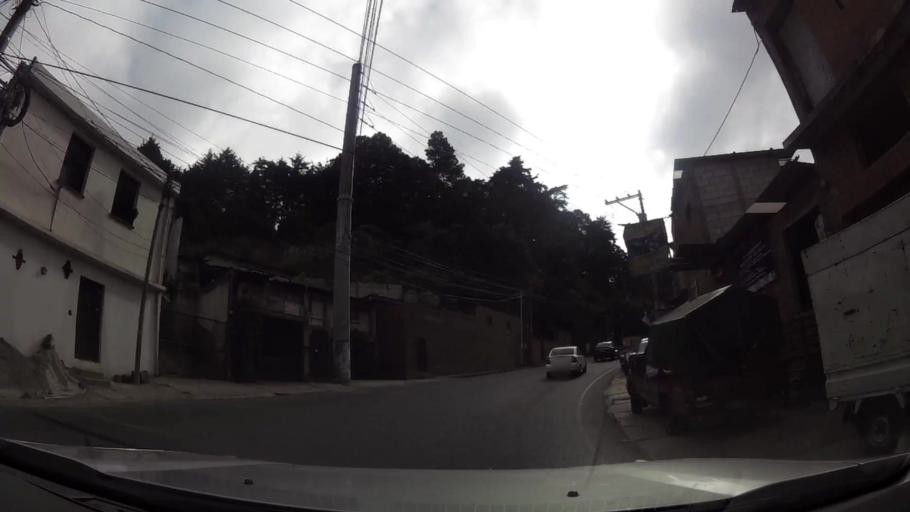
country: GT
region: Guatemala
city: Santa Catarina Pinula
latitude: 14.5633
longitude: -90.4790
